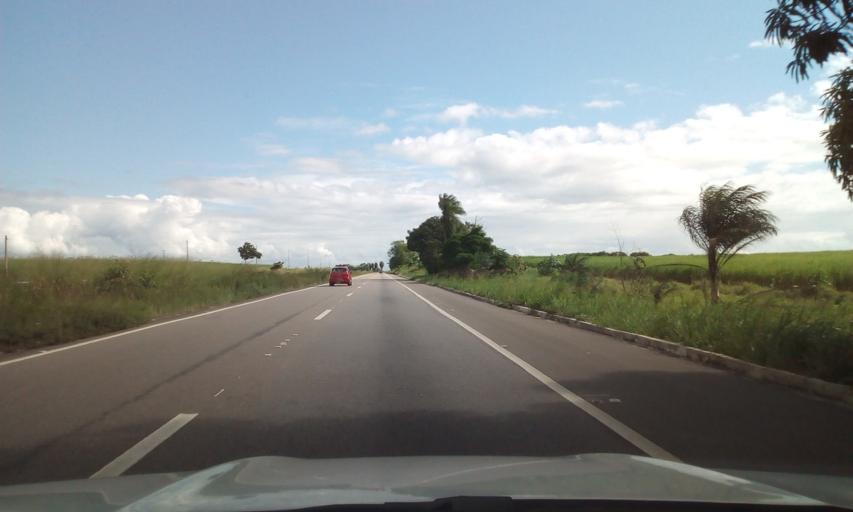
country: BR
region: Pernambuco
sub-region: Itapissuma
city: Itapissuma
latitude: -7.7161
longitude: -34.9368
